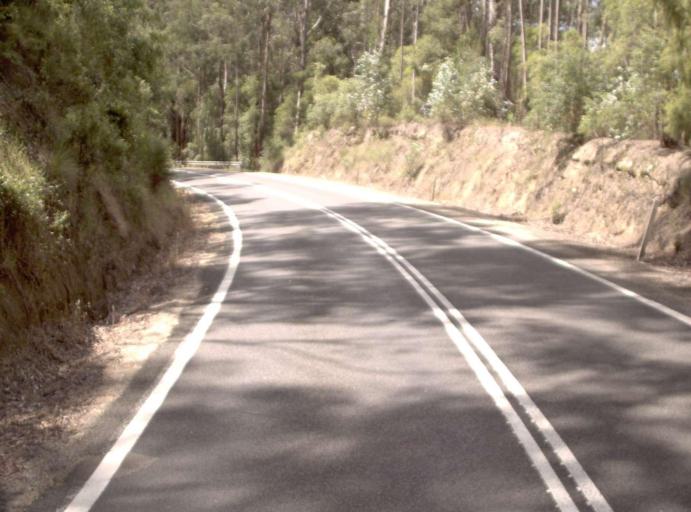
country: AU
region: New South Wales
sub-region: Bombala
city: Bombala
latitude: -37.5523
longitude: 149.3589
